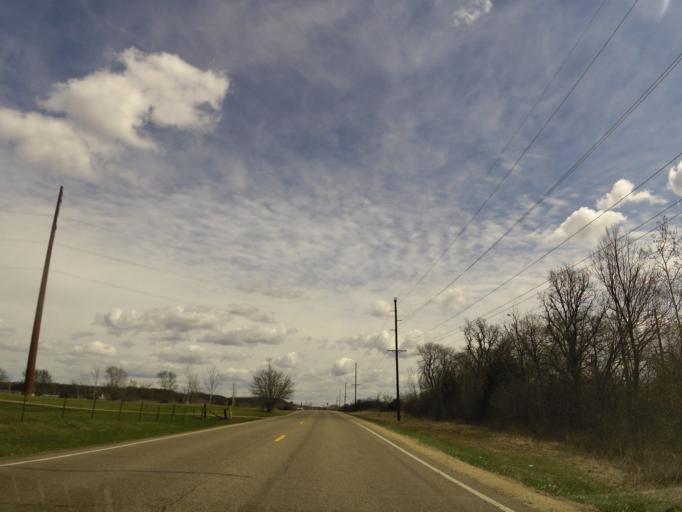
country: US
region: Minnesota
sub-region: Goodhue County
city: Cannon Falls
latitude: 44.5216
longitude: -92.9275
